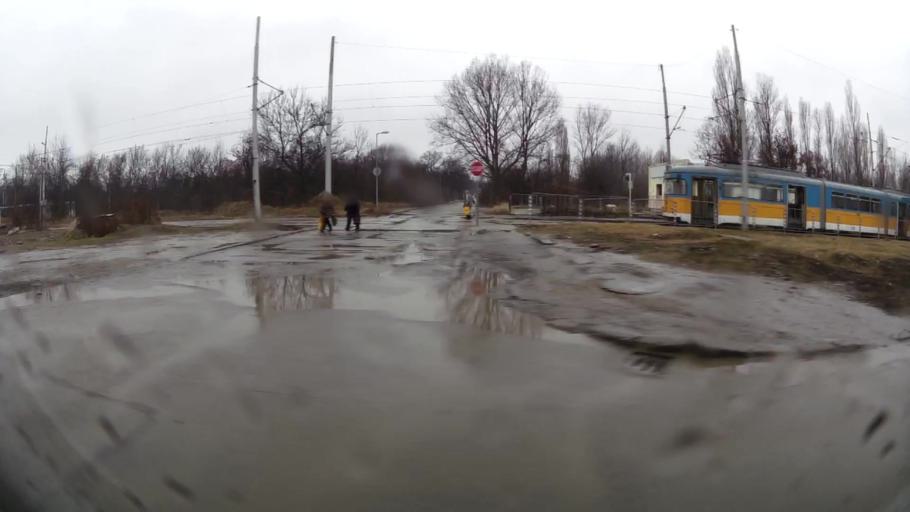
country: BG
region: Sofia-Capital
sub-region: Stolichna Obshtina
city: Sofia
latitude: 42.6639
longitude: 23.4115
